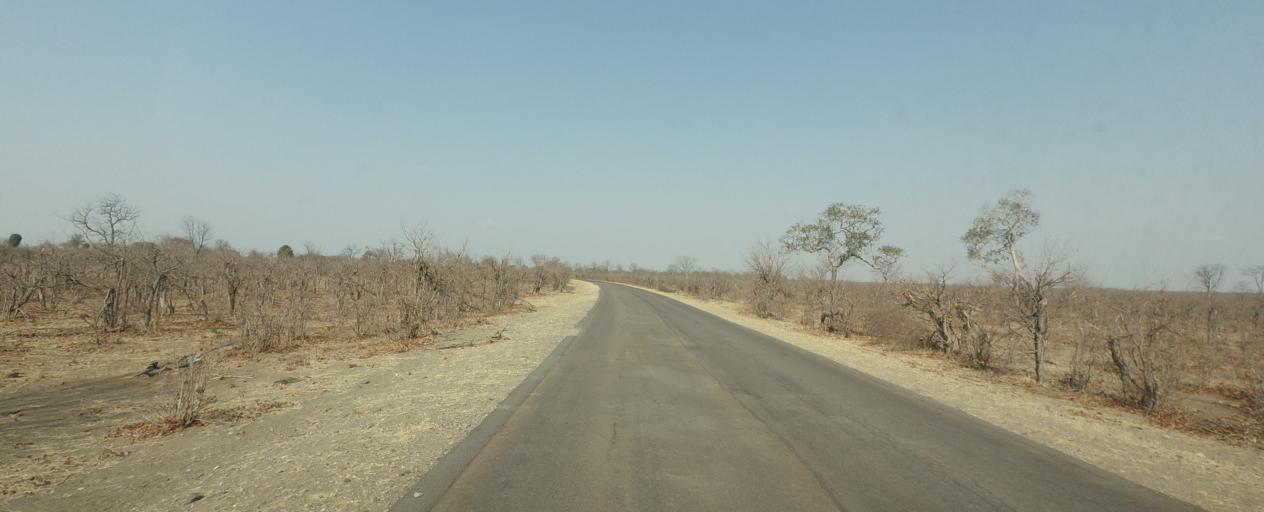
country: ZA
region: Limpopo
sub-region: Mopani District Municipality
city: Giyani
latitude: -23.0979
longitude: 31.4089
